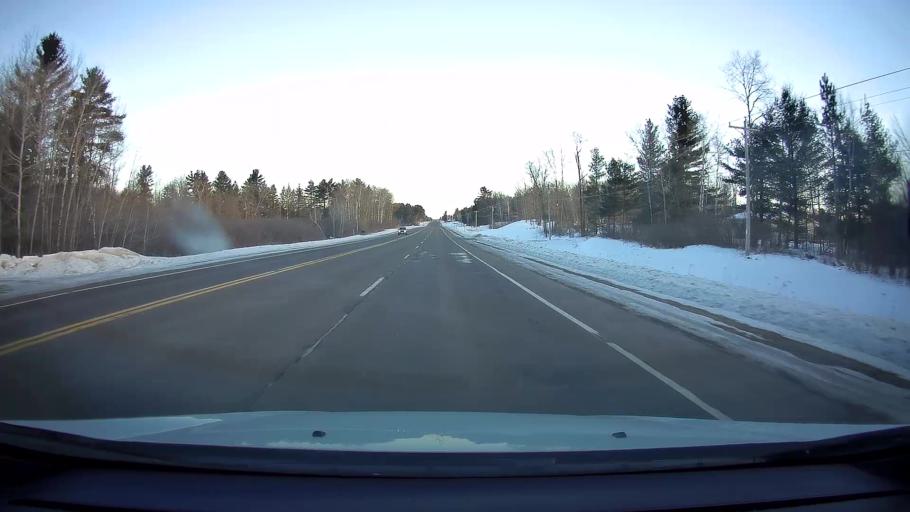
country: US
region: Wisconsin
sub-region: Barron County
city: Cumberland
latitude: 45.5639
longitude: -92.0173
